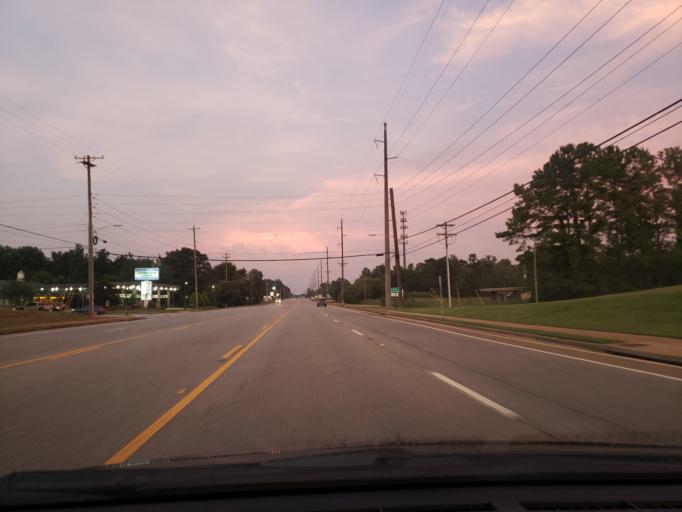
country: US
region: Georgia
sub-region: Dougherty County
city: Albany
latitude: 31.5856
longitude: -84.2385
